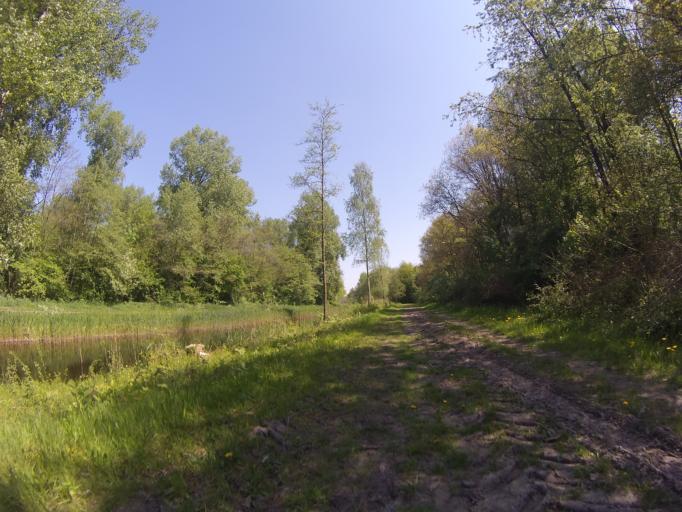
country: NL
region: Flevoland
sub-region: Gemeente Zeewolde
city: Zeewolde
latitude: 52.3170
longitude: 5.5281
